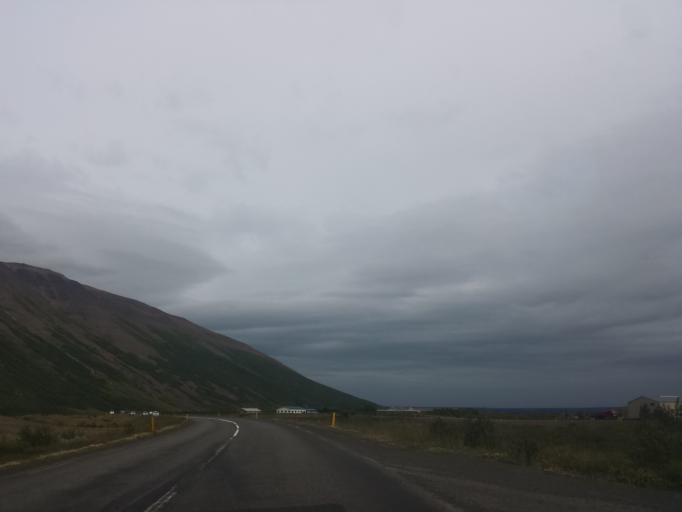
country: IS
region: Northeast
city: Akureyri
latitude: 65.7144
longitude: -17.7457
